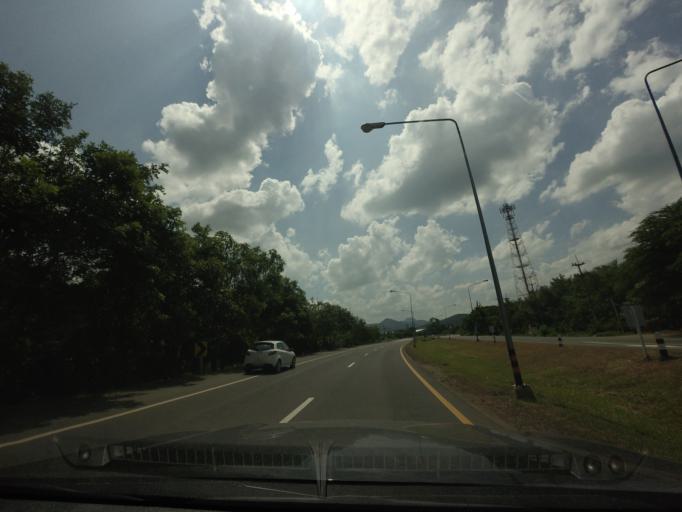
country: TH
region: Phetchabun
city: Phetchabun
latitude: 16.2694
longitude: 101.0567
